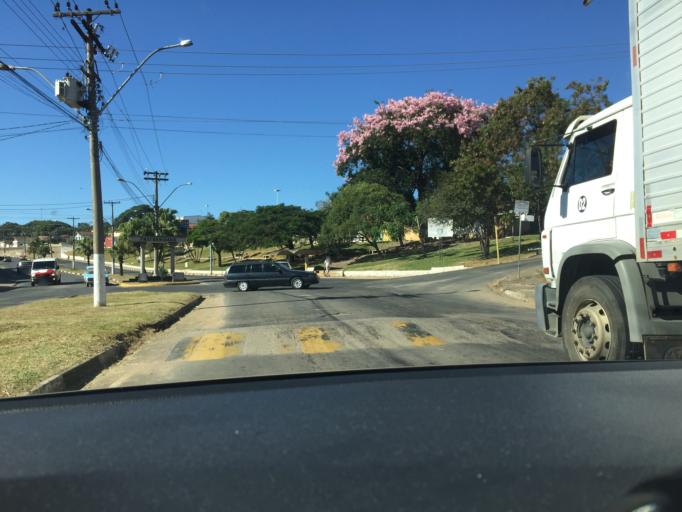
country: BR
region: Sao Paulo
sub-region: Santo Antonio Do Jardim
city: Espirito Santo do Pinhal
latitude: -22.1956
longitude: -46.7680
